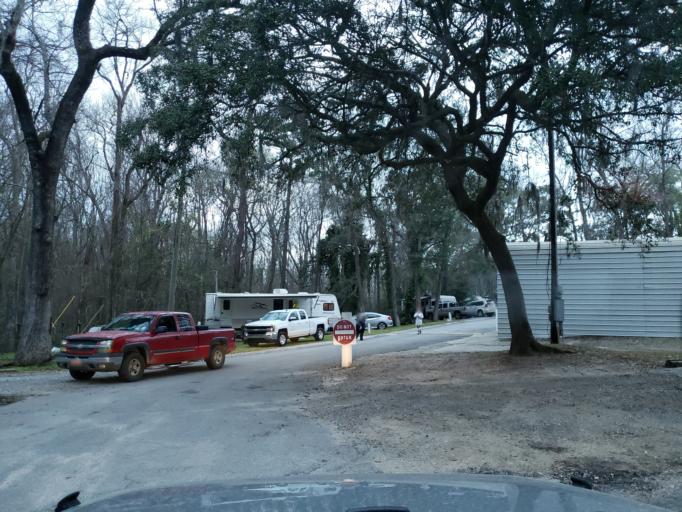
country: US
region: Georgia
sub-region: Bryan County
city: Richmond Hill
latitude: 32.0254
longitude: -81.3200
